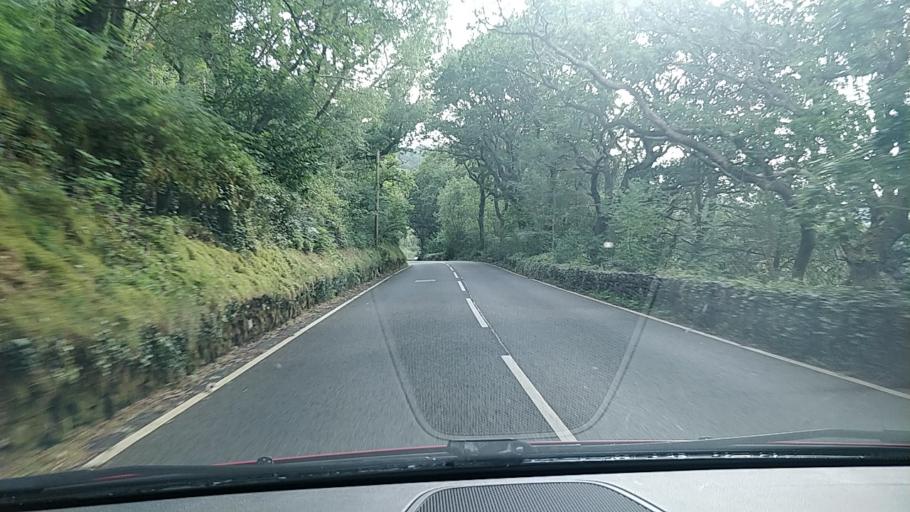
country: GB
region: Wales
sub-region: Gwynedd
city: Maentwrog
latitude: 52.9393
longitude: -3.9999
